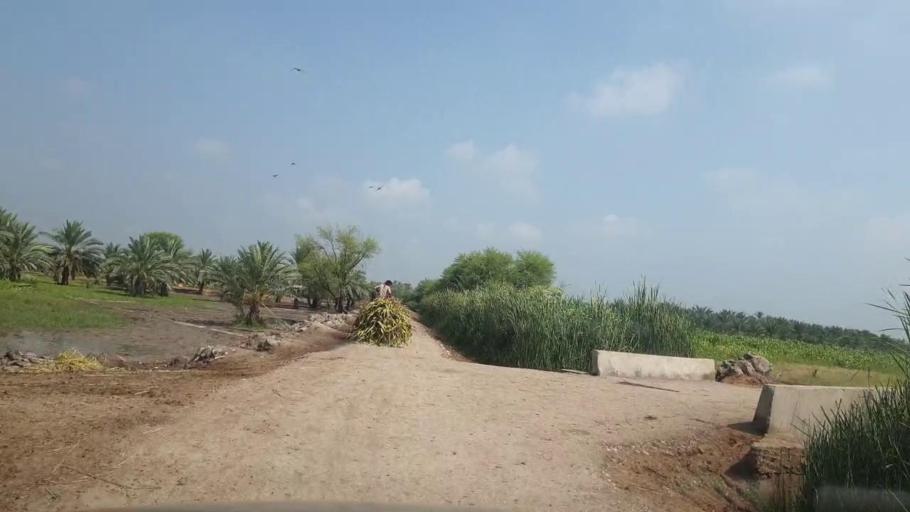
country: PK
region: Sindh
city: Pir jo Goth
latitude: 27.5994
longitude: 68.6932
